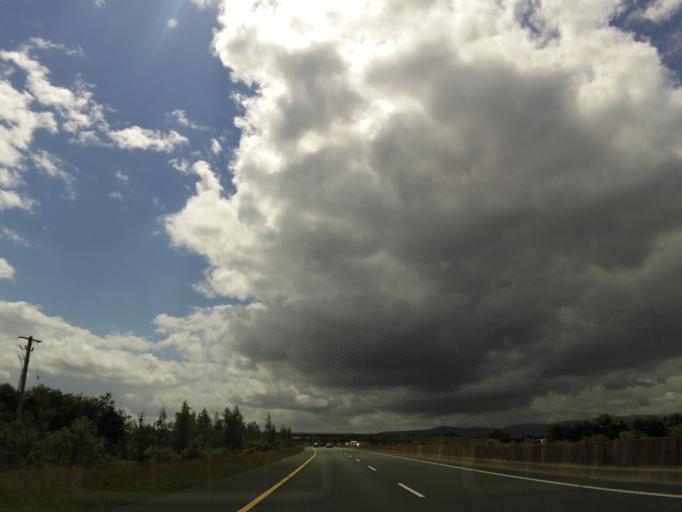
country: IE
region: Munster
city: Cashel
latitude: 52.4834
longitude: -7.9048
